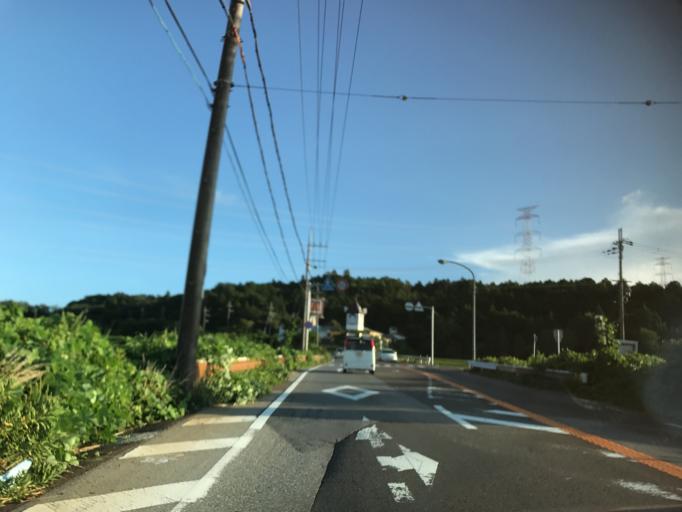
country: JP
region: Shiga Prefecture
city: Youkaichi
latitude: 35.0740
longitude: 136.2480
